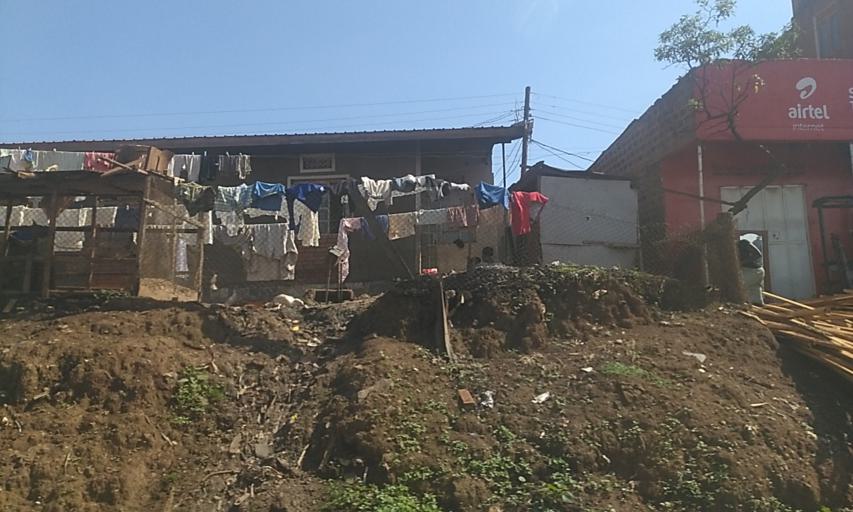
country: UG
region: Central Region
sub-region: Wakiso District
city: Kireka
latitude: 0.3442
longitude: 32.6409
